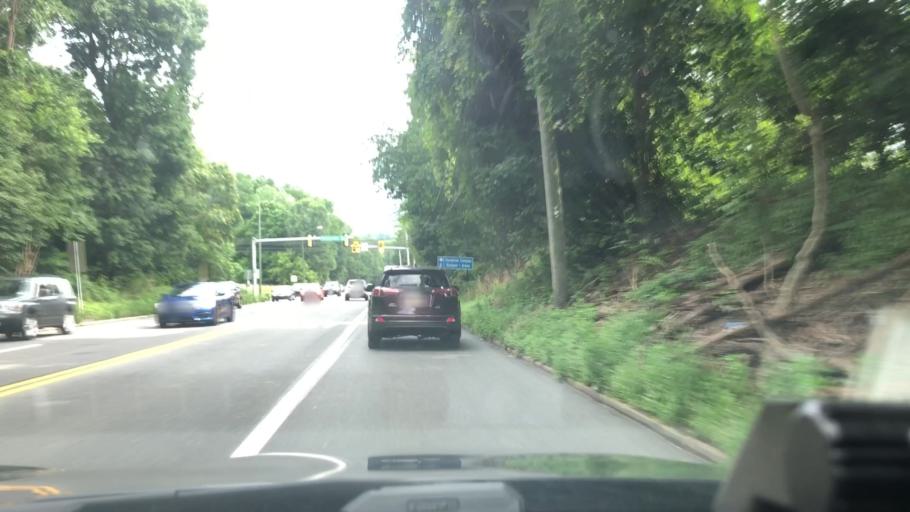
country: US
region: Pennsylvania
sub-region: Lehigh County
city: Fountain Hill
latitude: 40.5918
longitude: -75.3883
